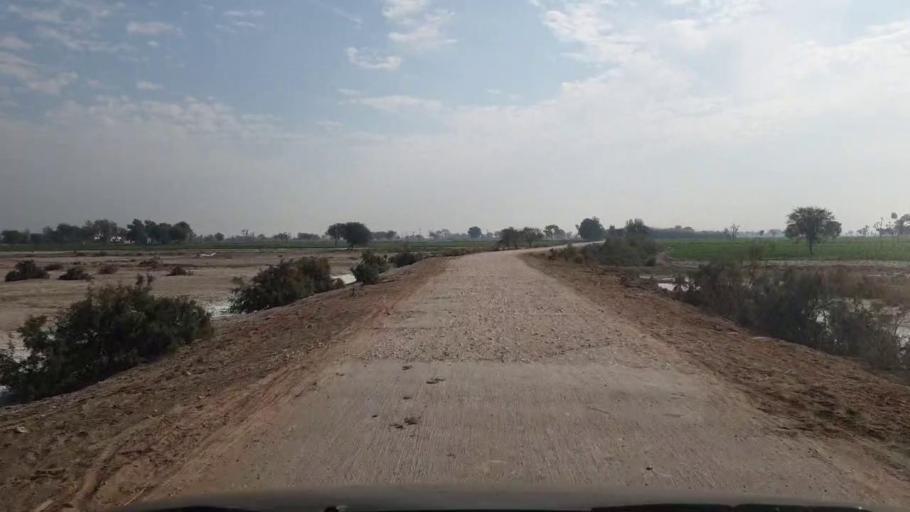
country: PK
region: Sindh
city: Hala
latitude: 25.9937
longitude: 68.4296
